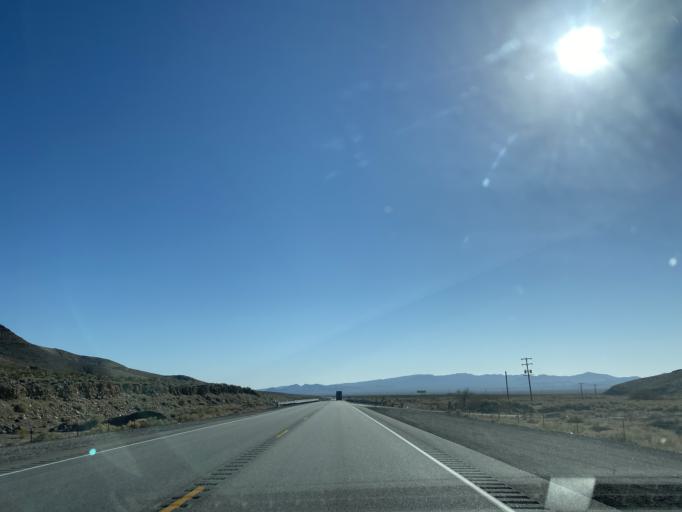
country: US
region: Nevada
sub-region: Nye County
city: Beatty
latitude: 36.8824
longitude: -116.7523
